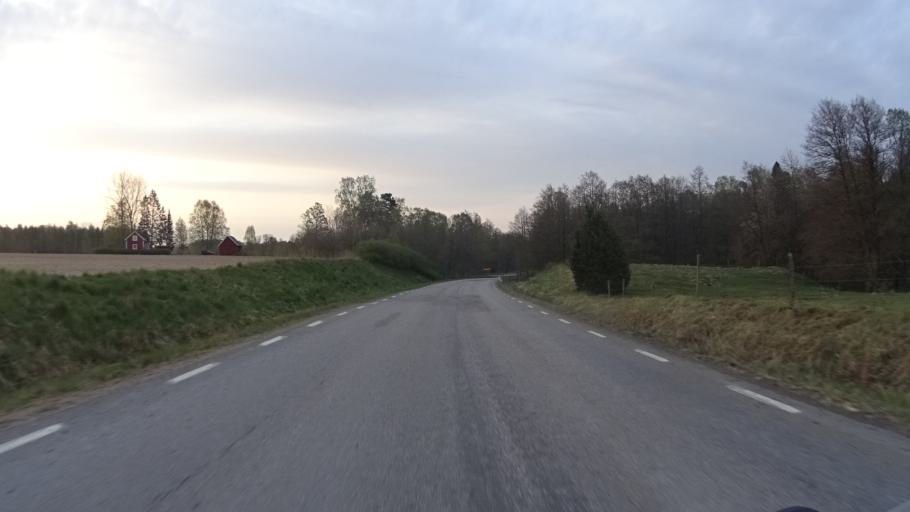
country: SE
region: Vaestra Goetaland
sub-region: Lidkopings Kommun
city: Vinninga
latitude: 58.4306
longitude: 13.3464
